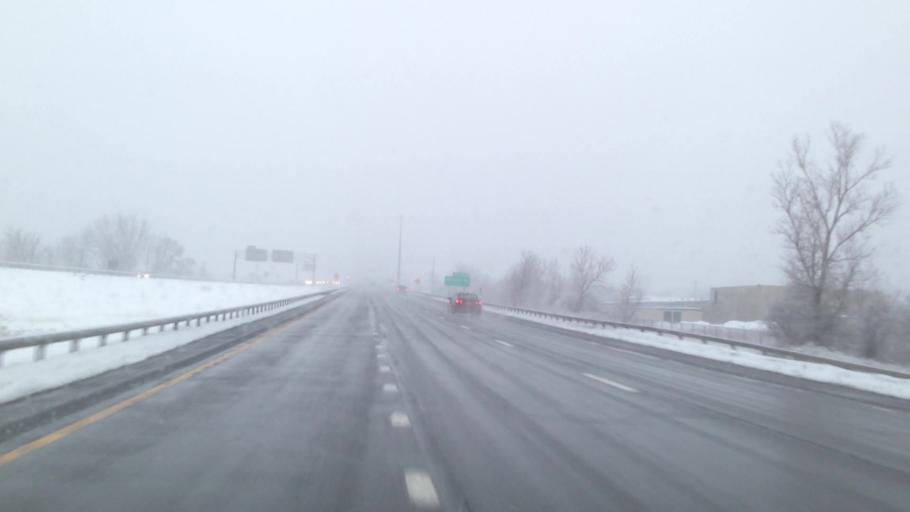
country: US
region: New York
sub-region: Onondaga County
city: East Syracuse
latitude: 43.0598
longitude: -76.0513
